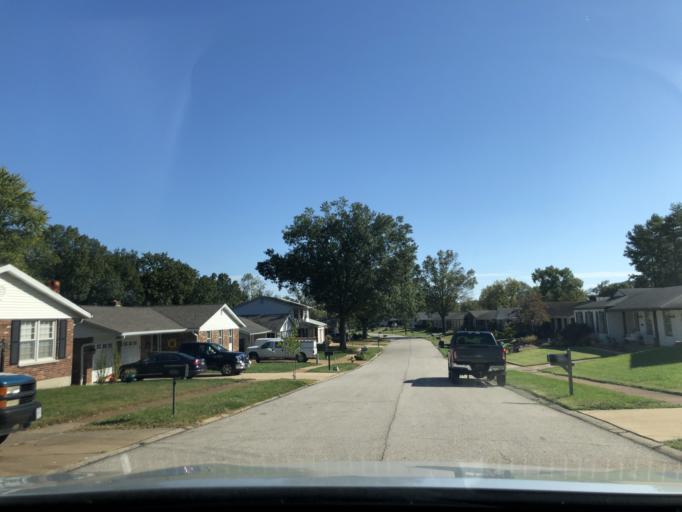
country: US
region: Missouri
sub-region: Saint Louis County
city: Concord
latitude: 38.5037
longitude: -90.3752
